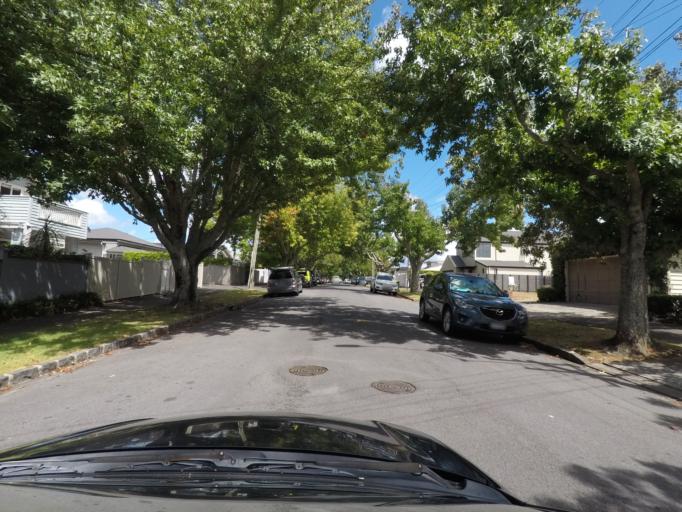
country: NZ
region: Auckland
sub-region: Auckland
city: Rosebank
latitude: -36.8570
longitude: 174.7068
